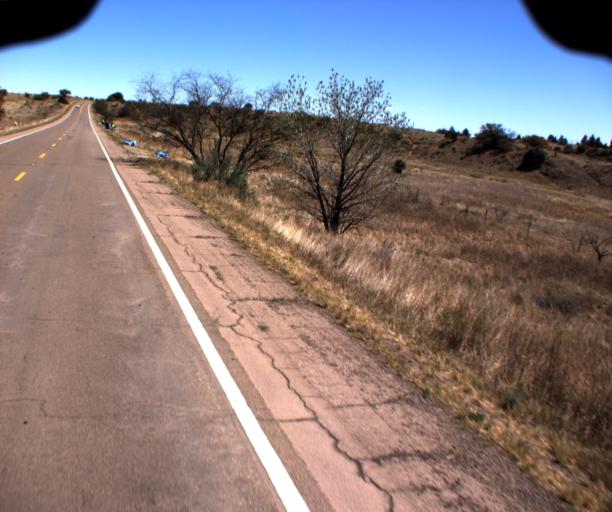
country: US
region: Arizona
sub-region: Pima County
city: Corona de Tucson
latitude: 31.6721
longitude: -110.6716
